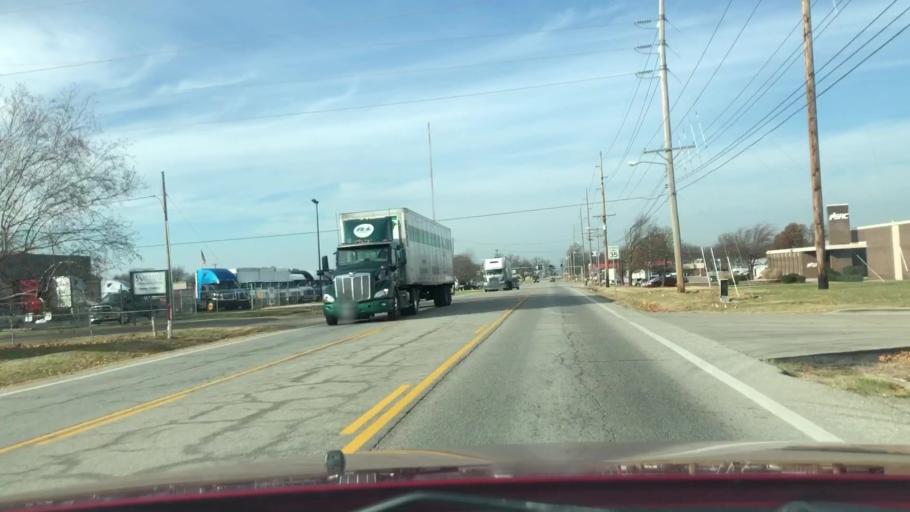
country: US
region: Missouri
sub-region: Greene County
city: Springfield
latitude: 37.2245
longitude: -93.2314
